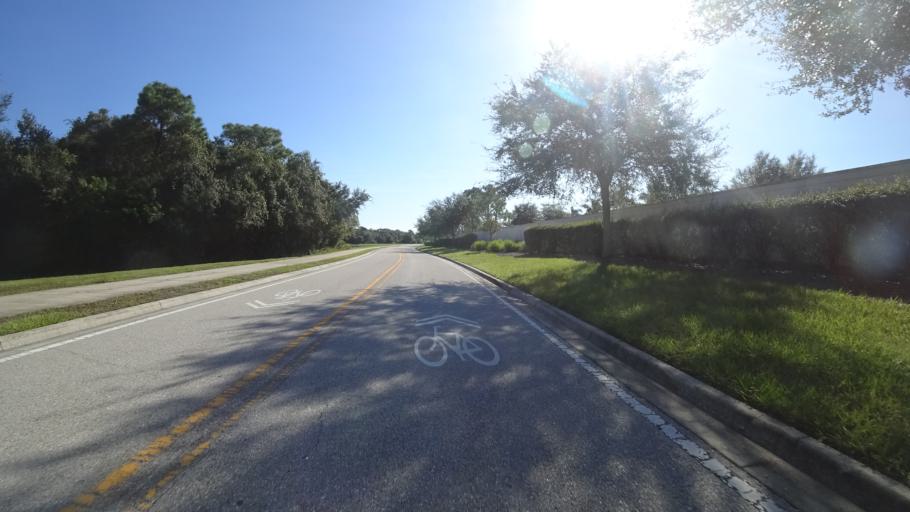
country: US
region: Florida
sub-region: Sarasota County
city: The Meadows
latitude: 27.4178
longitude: -82.4040
